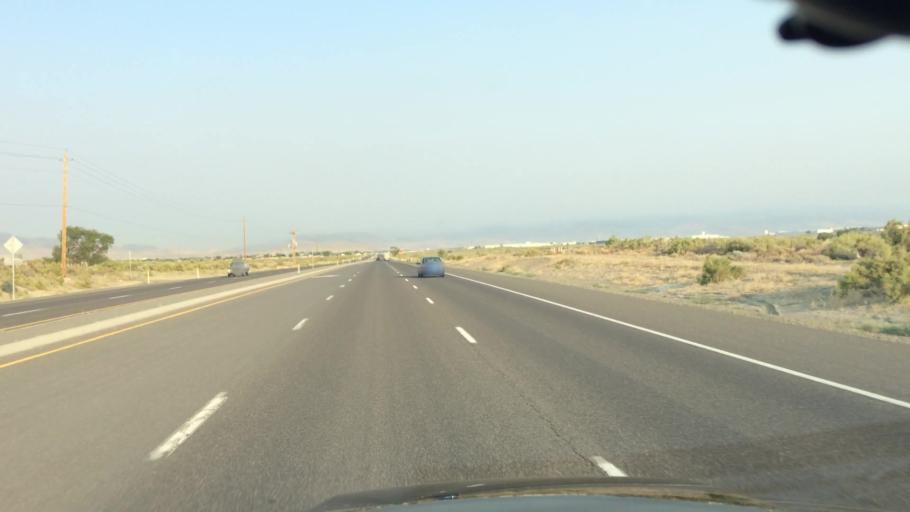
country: US
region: Nevada
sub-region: Lyon County
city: Fernley
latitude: 39.5947
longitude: -119.1696
